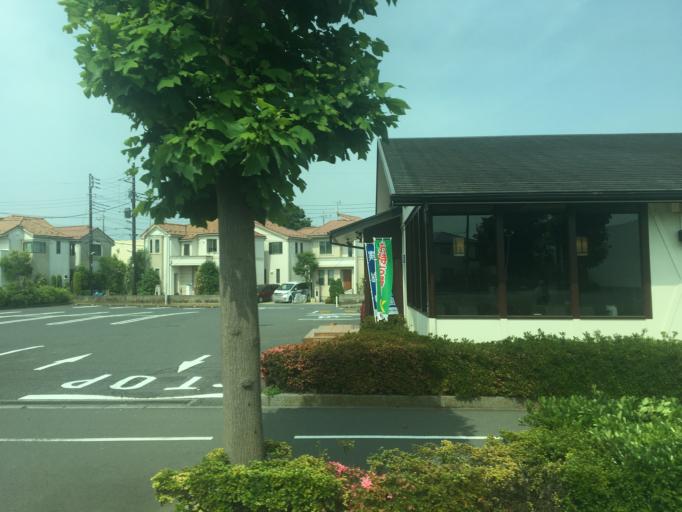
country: JP
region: Saitama
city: Shiki
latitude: 35.8123
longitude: 139.5709
